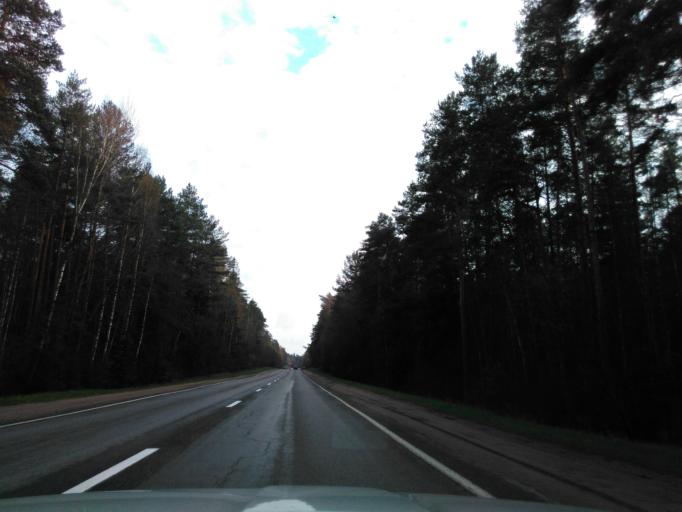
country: BY
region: Minsk
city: Plyeshchanitsy
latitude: 54.3656
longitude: 27.8836
